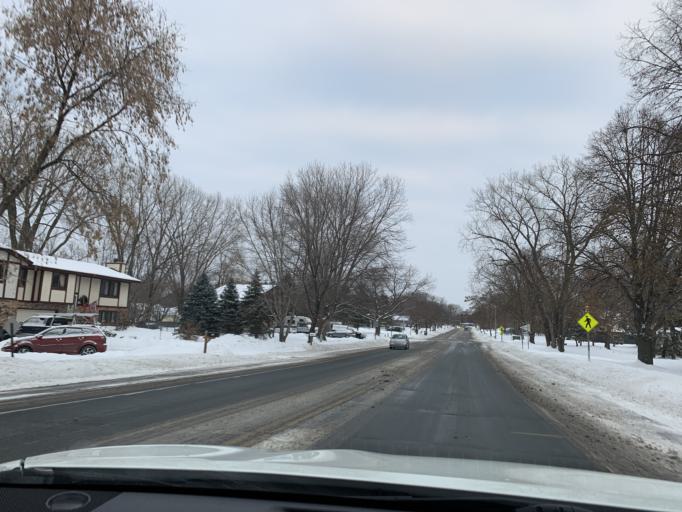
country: US
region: Minnesota
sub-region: Anoka County
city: Coon Rapids
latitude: 45.1638
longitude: -93.2833
